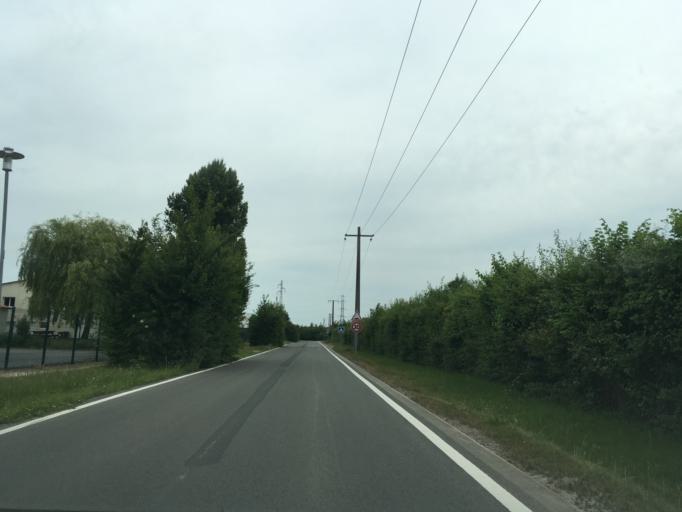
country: FR
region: Poitou-Charentes
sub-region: Departement des Deux-Sevres
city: Bessines
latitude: 46.3050
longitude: -0.4835
